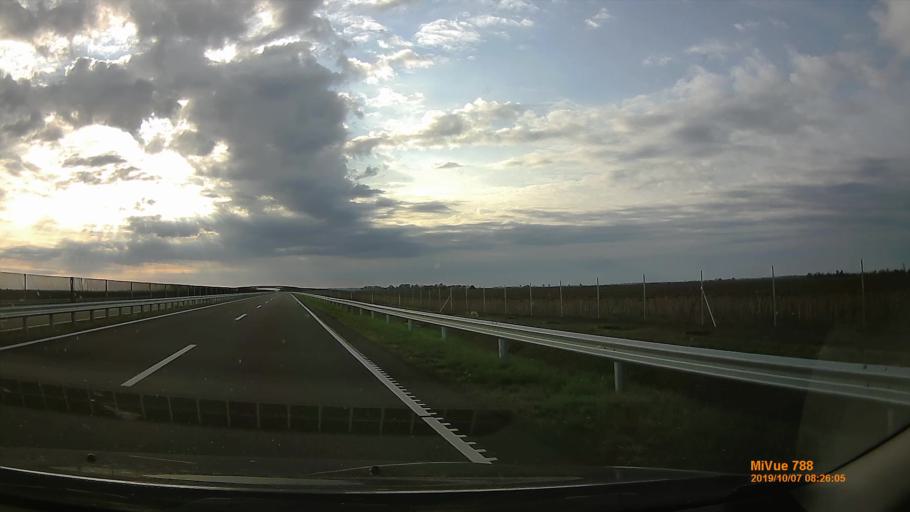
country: HU
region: Jasz-Nagykun-Szolnok
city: Kunszentmarton
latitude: 46.8242
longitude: 20.3651
